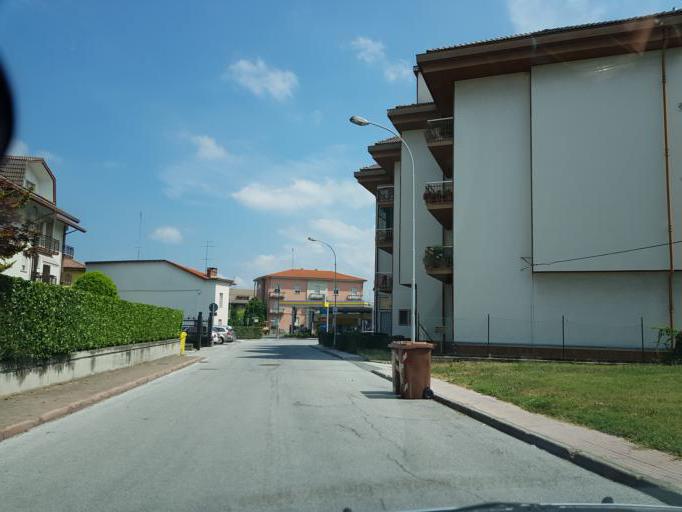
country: IT
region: Piedmont
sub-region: Provincia di Cuneo
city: Borgo San Dalmazzo
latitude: 44.3331
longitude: 7.4889
